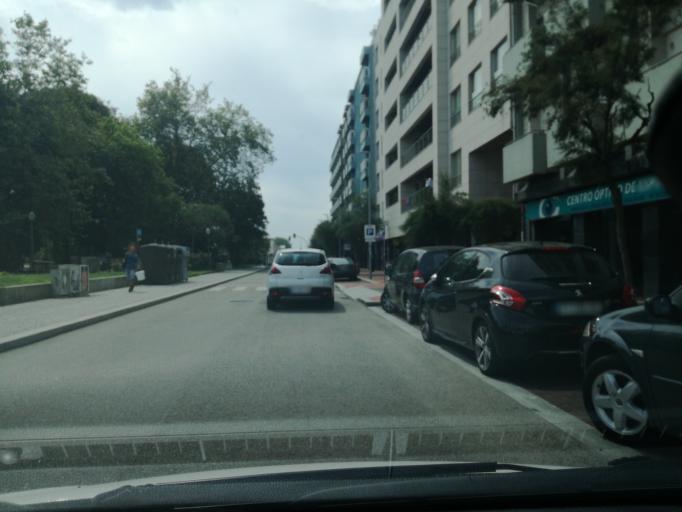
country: PT
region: Aveiro
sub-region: Espinho
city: Espinho
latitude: 41.0085
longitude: -8.6398
